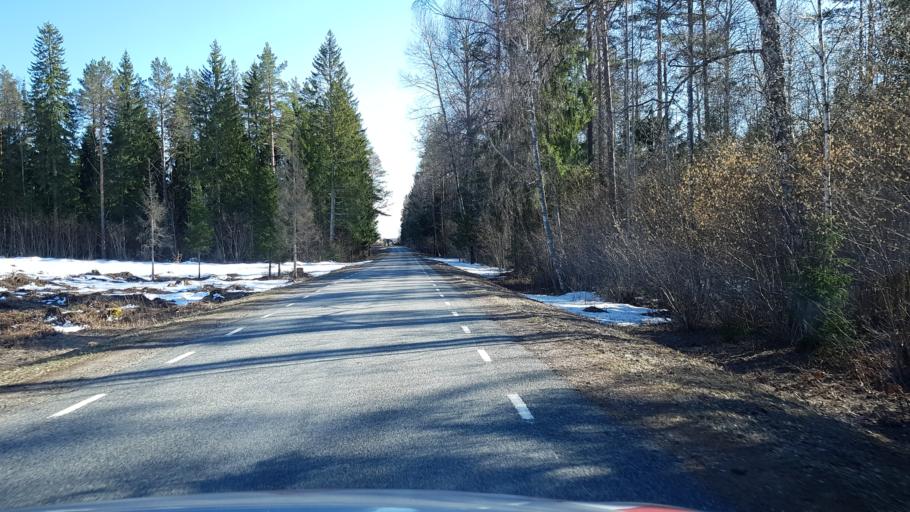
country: EE
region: Laeaene-Virumaa
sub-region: Kadrina vald
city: Kadrina
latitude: 59.3881
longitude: 26.0220
